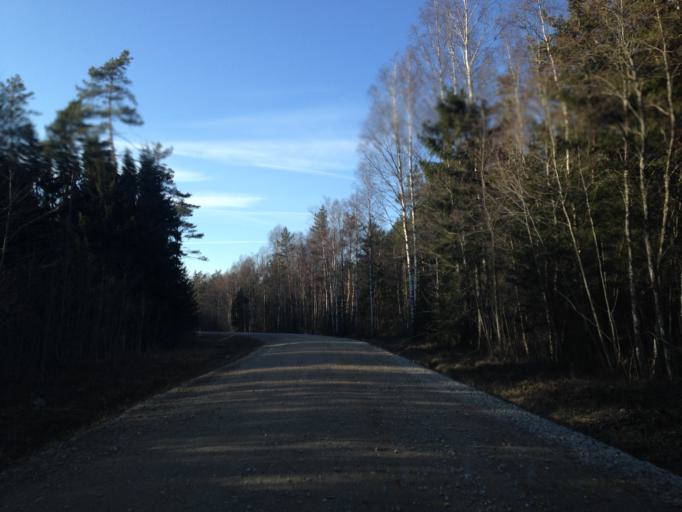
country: EE
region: Harju
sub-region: Nissi vald
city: Turba
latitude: 59.1707
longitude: 24.1375
